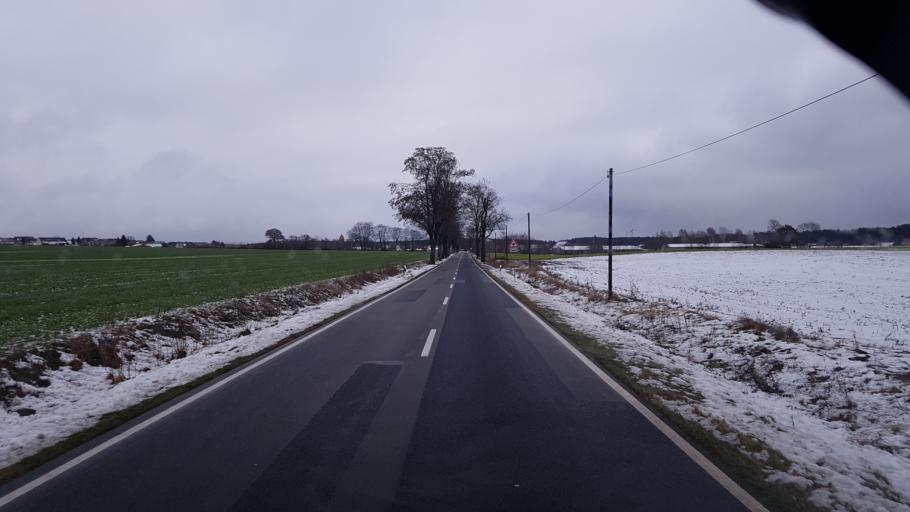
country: DE
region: Brandenburg
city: Tauer
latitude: 51.9784
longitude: 14.5233
